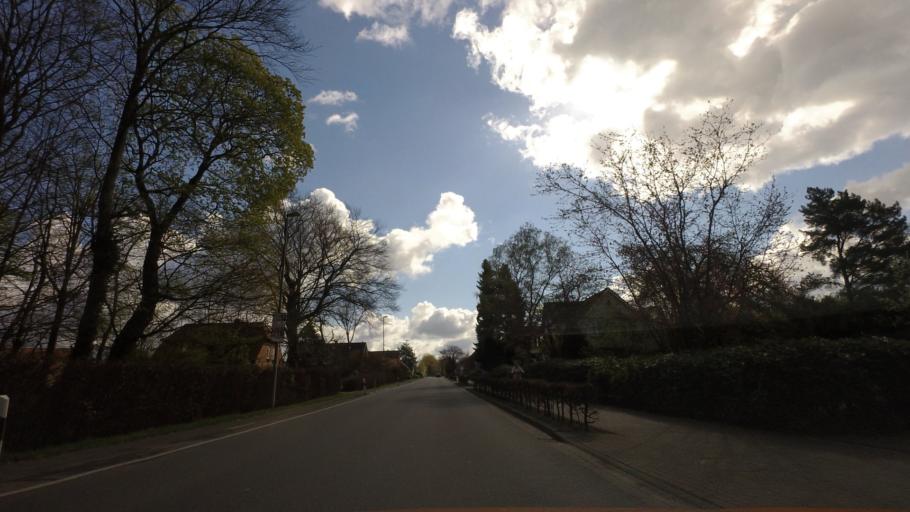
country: DE
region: Lower Saxony
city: Ganderkesee
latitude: 53.0478
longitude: 8.4920
